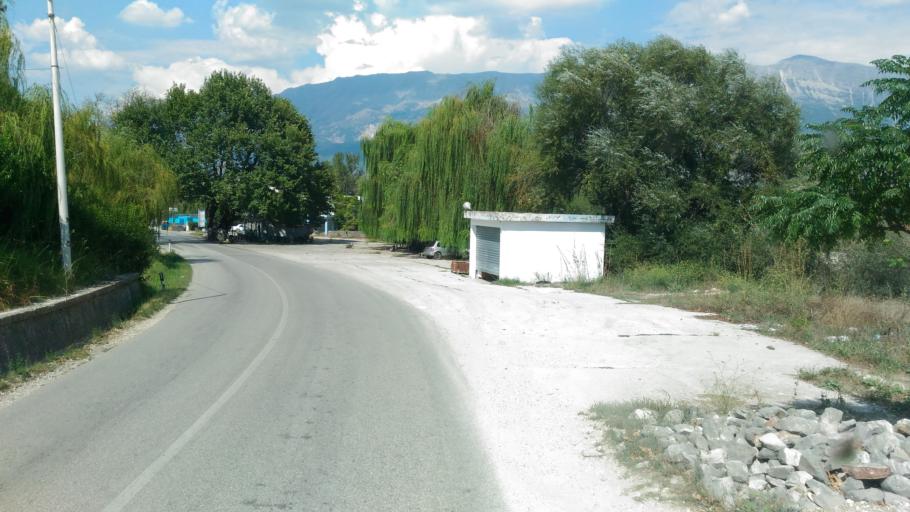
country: AL
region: Gjirokaster
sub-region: Rrethi i Gjirokastres
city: Dervician
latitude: 40.0606
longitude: 20.1727
